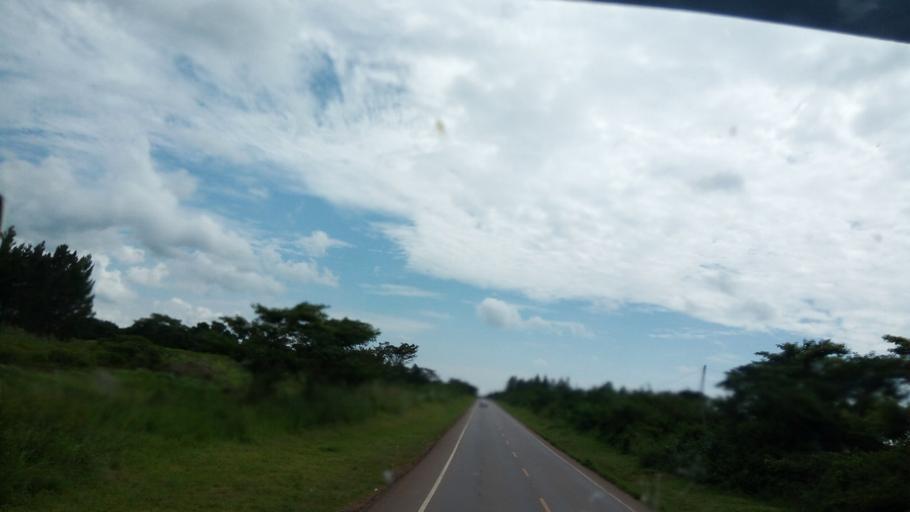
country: UG
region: Central Region
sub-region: Nakasongola District
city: Nakasongola
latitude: 1.2080
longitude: 32.4636
